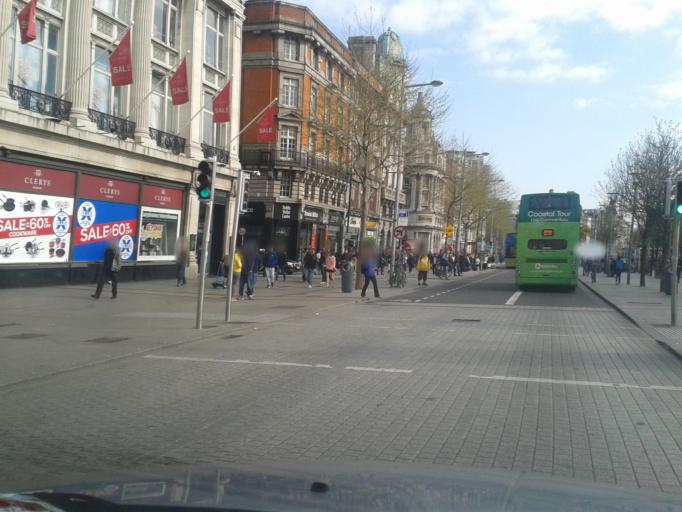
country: IE
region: Leinster
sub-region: Dublin City
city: Dublin
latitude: 53.3491
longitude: -6.2599
